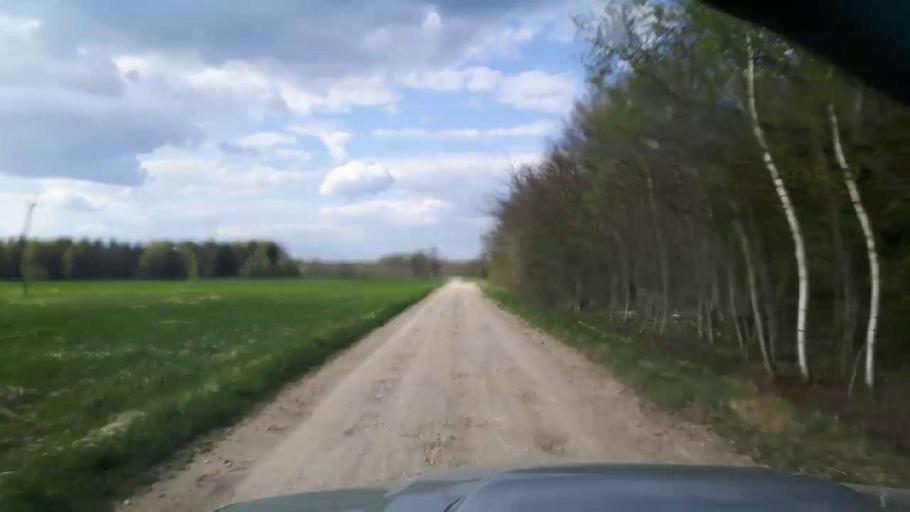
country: EE
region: Paernumaa
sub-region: Sindi linn
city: Sindi
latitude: 58.4421
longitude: 24.7574
